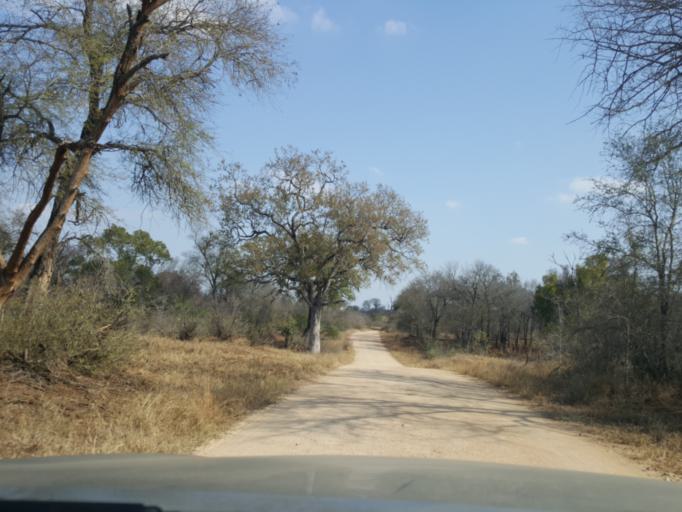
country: ZA
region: Mpumalanga
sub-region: Ehlanzeni District
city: Komatipoort
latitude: -25.2810
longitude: 31.7743
